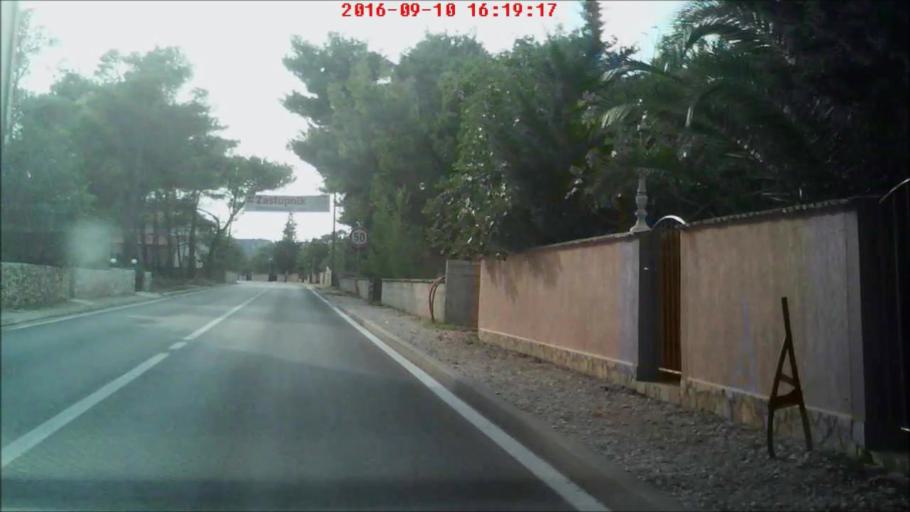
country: HR
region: Zadarska
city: Vir
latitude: 44.3001
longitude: 15.0953
